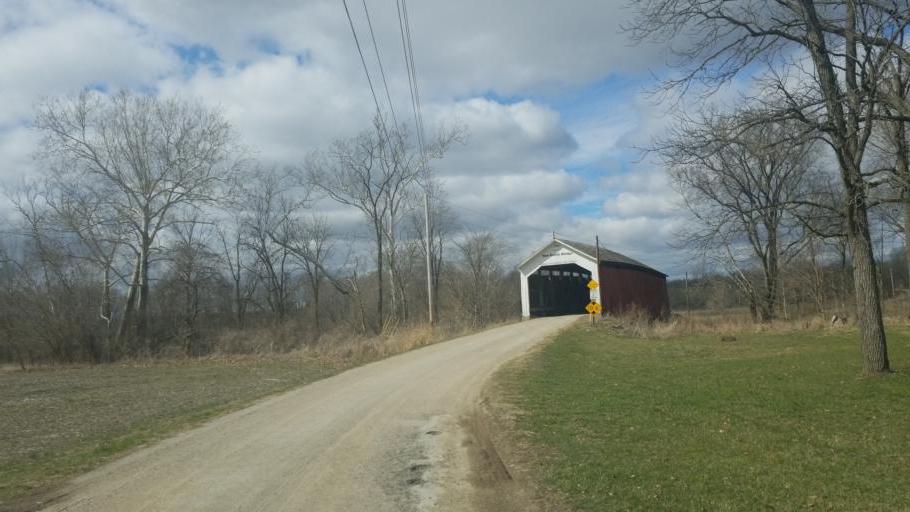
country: US
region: Indiana
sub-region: Parke County
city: Montezuma
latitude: 39.7731
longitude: -87.3307
